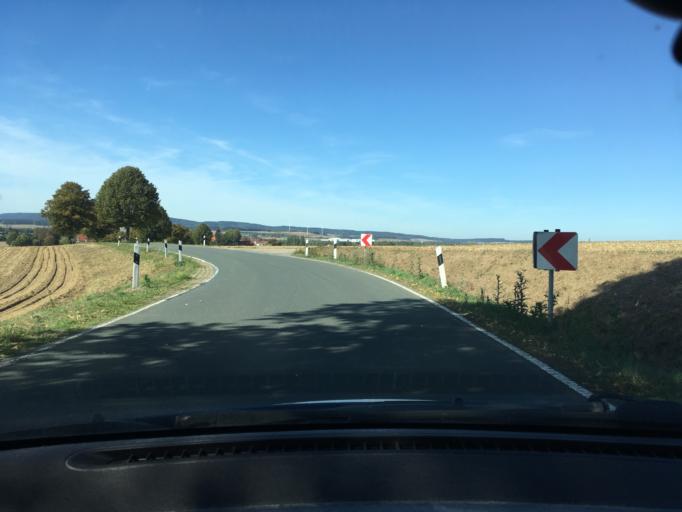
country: DE
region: Lower Saxony
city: Messenkamp
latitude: 52.2577
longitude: 9.3949
